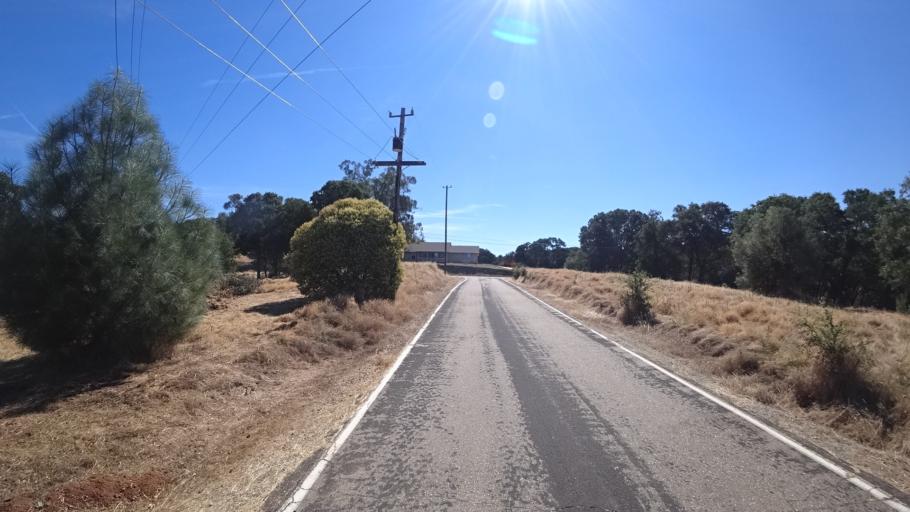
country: US
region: California
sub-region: Calaveras County
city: Valley Springs
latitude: 38.1658
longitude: -120.8463
